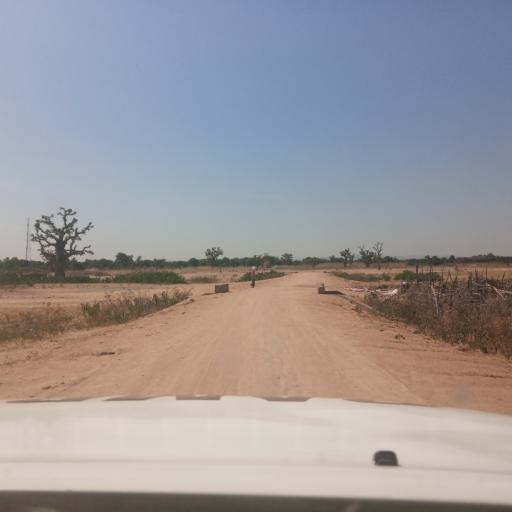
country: NG
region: Adamawa
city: Little Gombi
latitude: 9.7757
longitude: 12.5884
